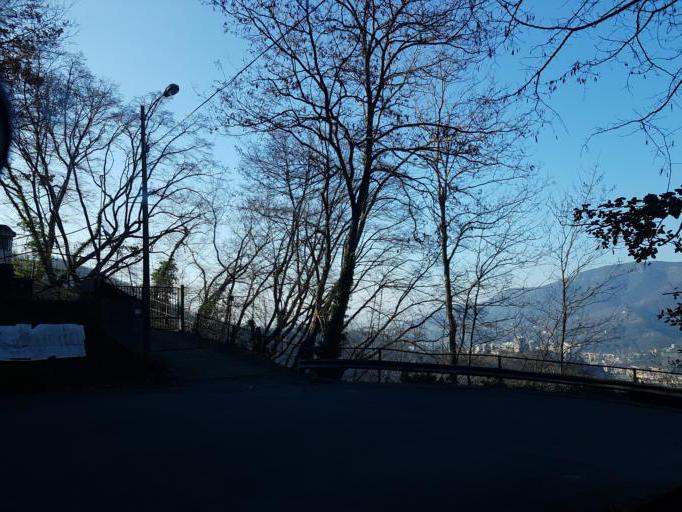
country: IT
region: Liguria
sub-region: Provincia di Genova
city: Manesseno
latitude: 44.4568
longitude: 8.9212
